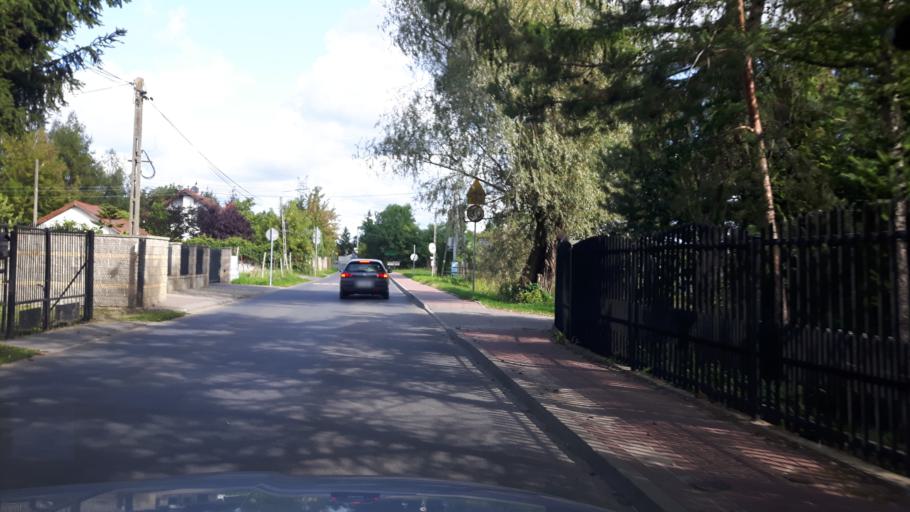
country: PL
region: Masovian Voivodeship
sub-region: Powiat legionowski
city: Stanislawow Pierwszy
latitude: 52.3739
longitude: 21.0402
